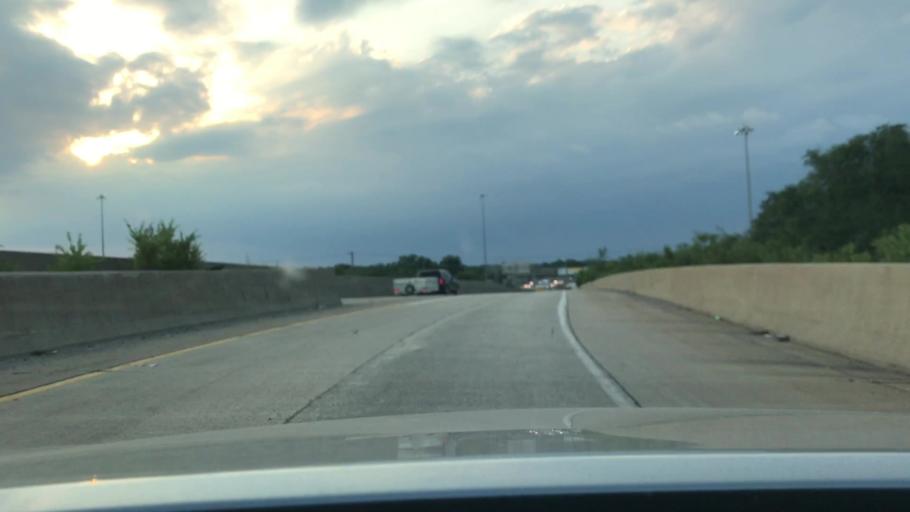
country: US
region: Illinois
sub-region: Cook County
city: Indian Head Park
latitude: 41.7612
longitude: -87.9024
